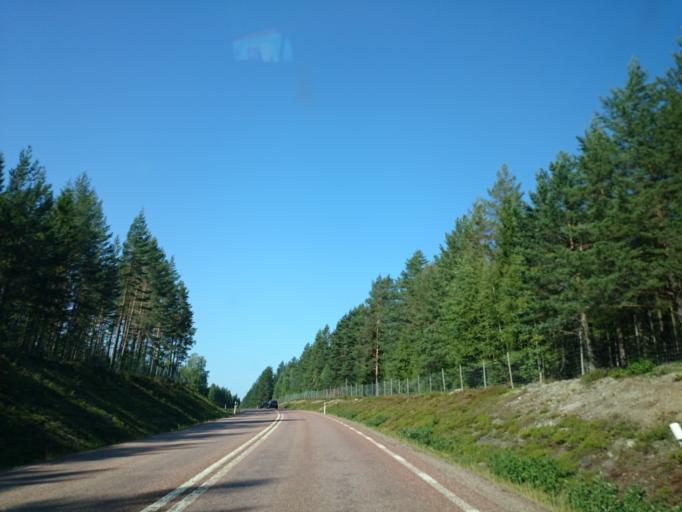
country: SE
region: Gaevleborg
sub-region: Hudiksvalls Kommun
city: Delsbo
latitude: 61.7644
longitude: 16.7590
